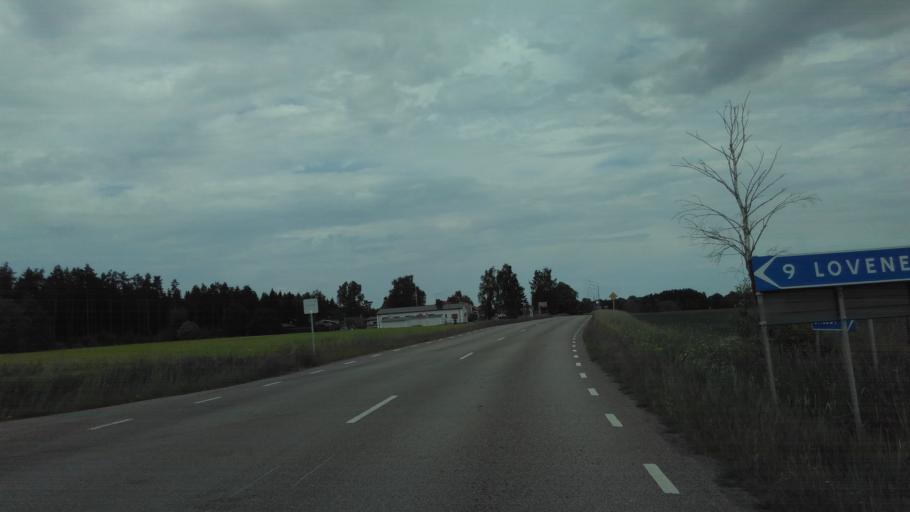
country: SE
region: Vaestra Goetaland
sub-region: Lidkopings Kommun
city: Lidkoping
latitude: 58.4320
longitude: 13.1587
